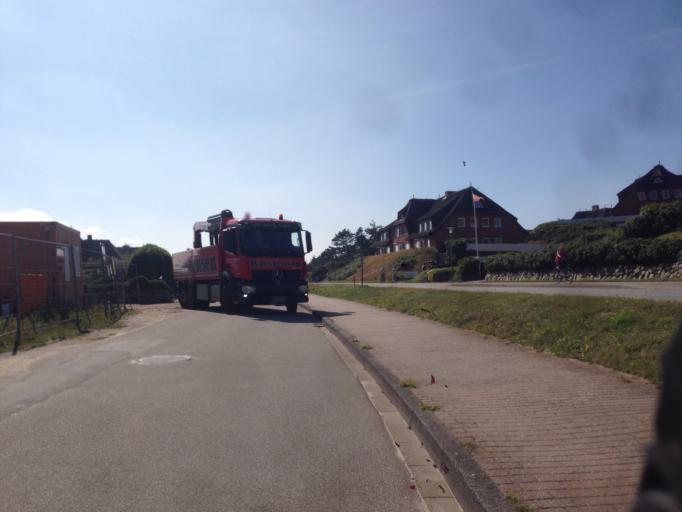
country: DE
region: Schleswig-Holstein
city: Westerland
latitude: 54.8435
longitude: 8.2928
